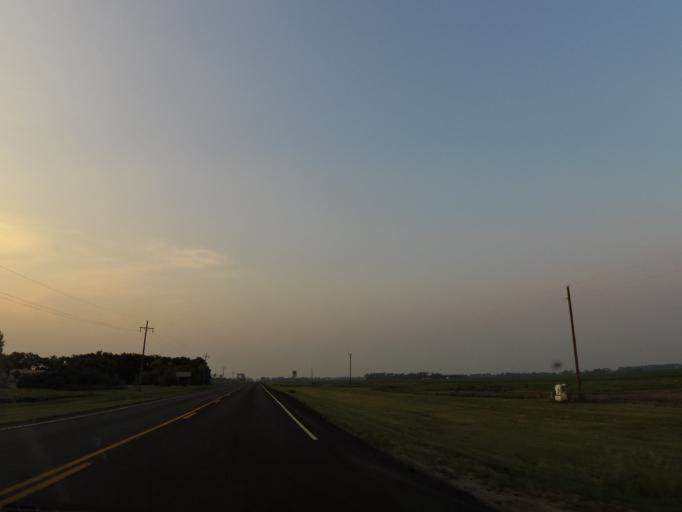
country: US
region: North Dakota
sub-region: Walsh County
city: Park River
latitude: 48.3107
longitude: -97.6224
